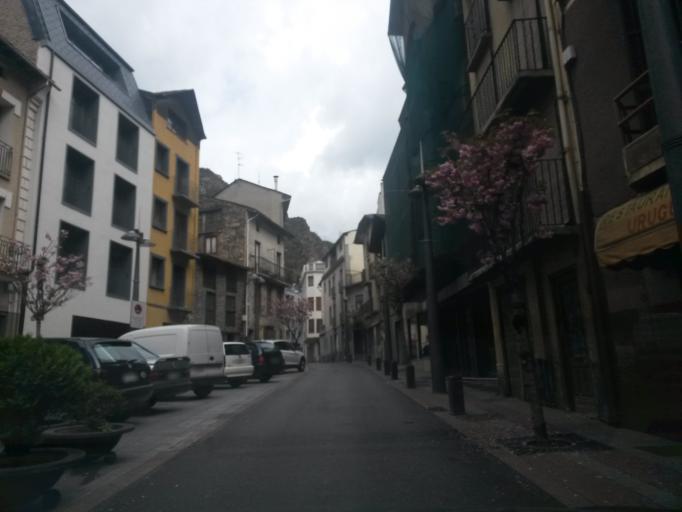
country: AD
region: Sant Julia de Loria
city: Sant Julia de Loria
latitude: 42.4629
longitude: 1.4911
